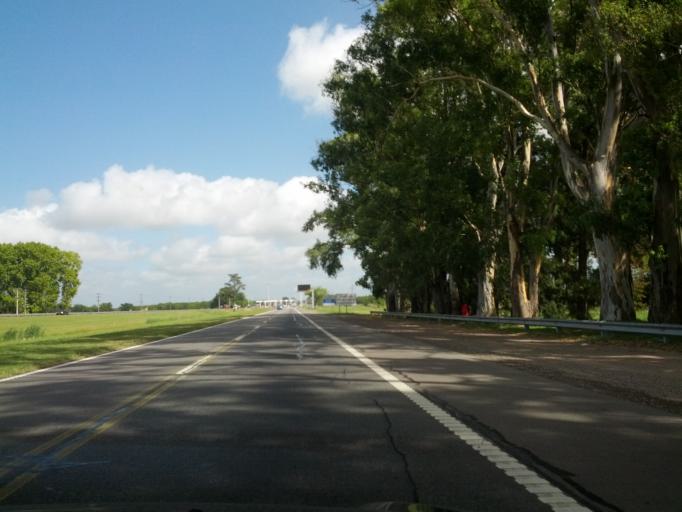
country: AR
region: Buenos Aires
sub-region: Partido de Mercedes
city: Mercedes
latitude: -34.6436
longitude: -59.2873
